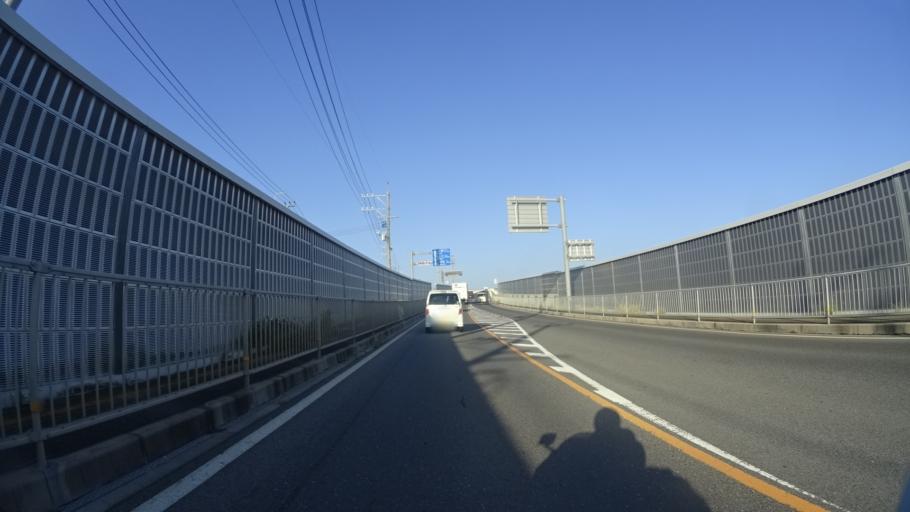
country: JP
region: Shimane
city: Sakaiminato
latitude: 35.5212
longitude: 133.2094
